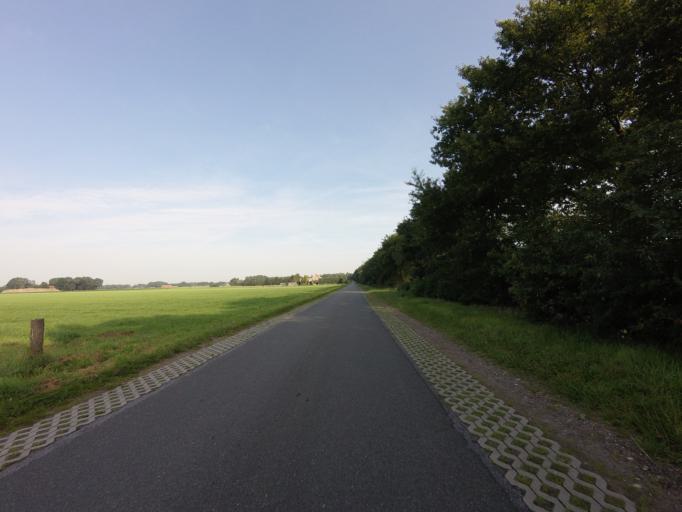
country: DE
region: Lower Saxony
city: Itterbeck
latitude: 52.4828
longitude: 6.8176
